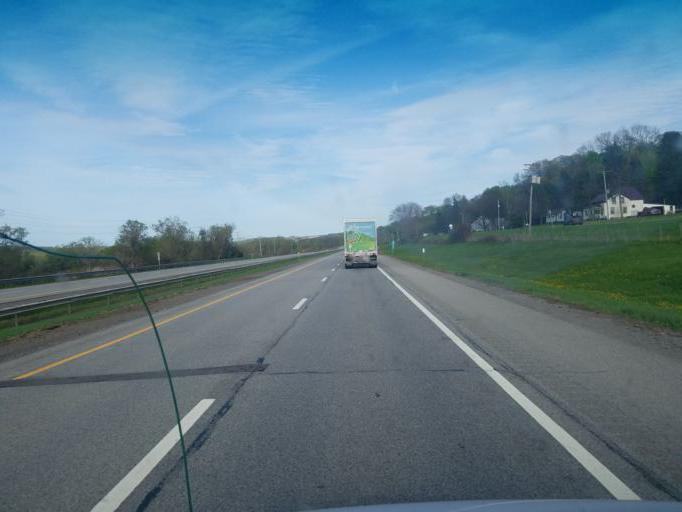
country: US
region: New York
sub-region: Herkimer County
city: Herkimer
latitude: 43.0141
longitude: -74.9386
